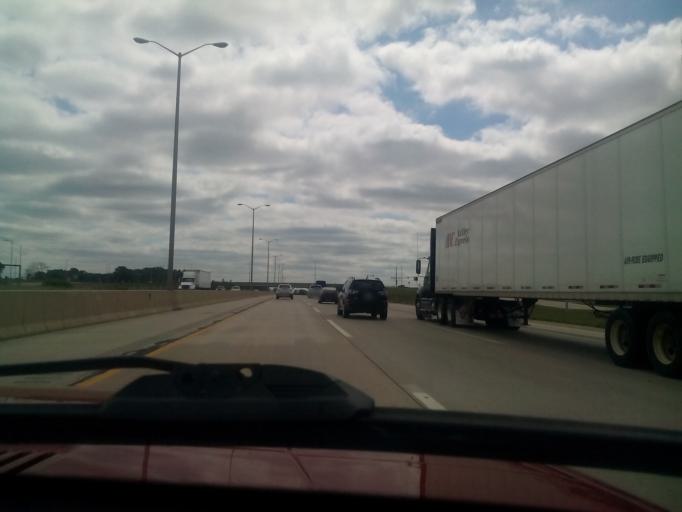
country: US
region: Illinois
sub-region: Cook County
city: Lemont
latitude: 41.6593
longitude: -88.0208
